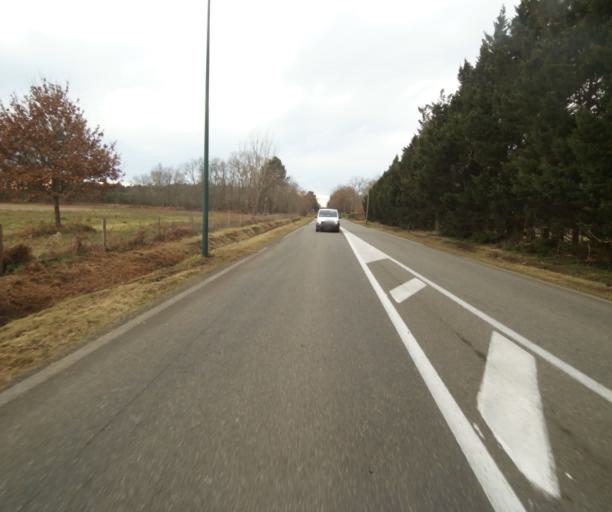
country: FR
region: Aquitaine
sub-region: Departement des Landes
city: Gabarret
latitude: 44.1017
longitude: -0.0153
